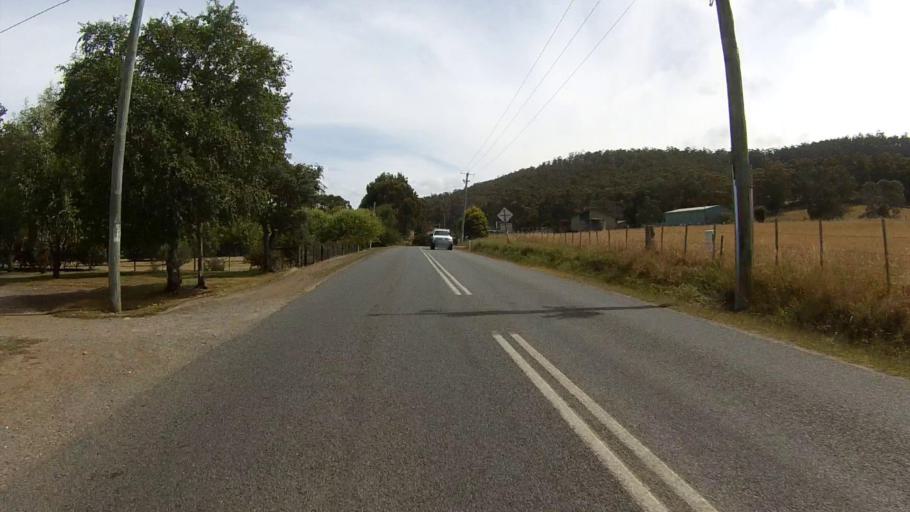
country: AU
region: Tasmania
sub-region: Huon Valley
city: Cygnet
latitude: -43.2090
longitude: 147.1157
